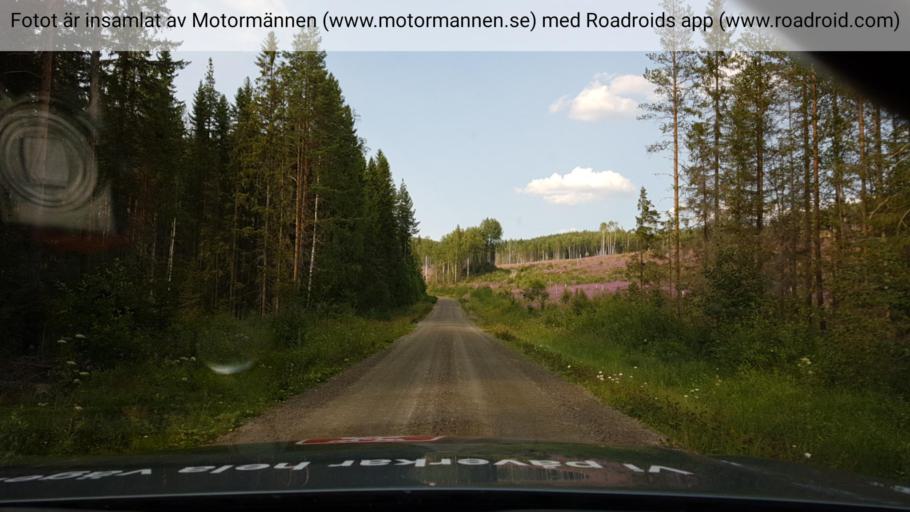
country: SE
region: Jaemtland
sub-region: Bergs Kommun
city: Hoverberg
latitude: 62.5260
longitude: 14.9148
